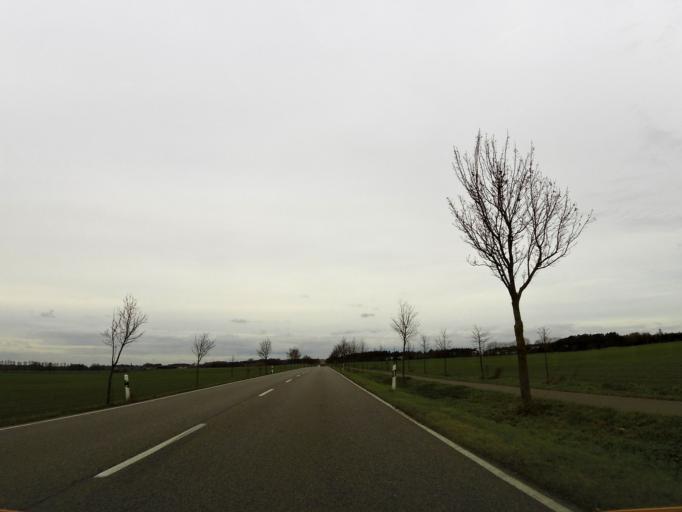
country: DE
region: Saxony-Anhalt
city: Pretzier
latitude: 52.8202
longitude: 11.2071
